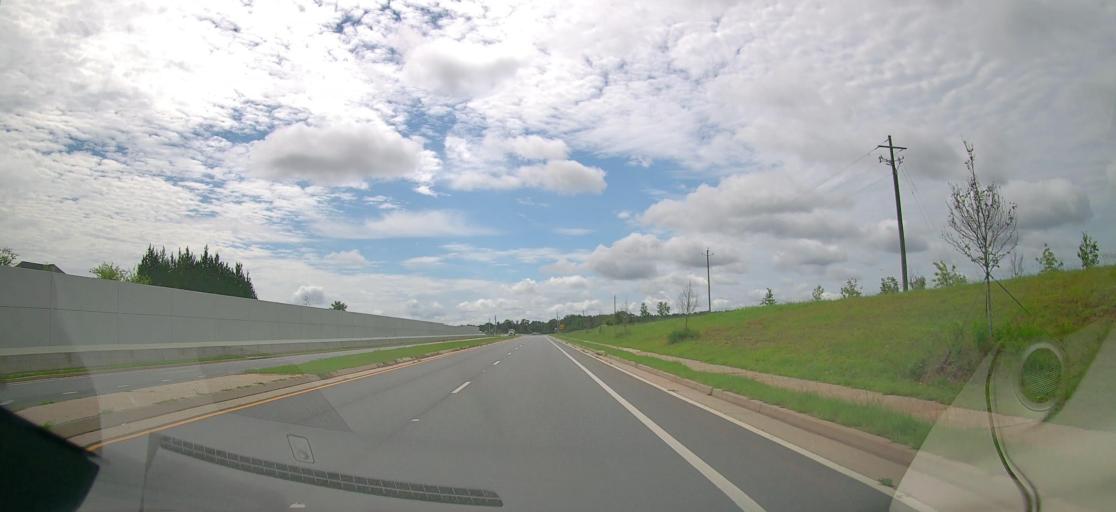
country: US
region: Georgia
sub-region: Houston County
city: Centerville
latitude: 32.7128
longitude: -83.6988
